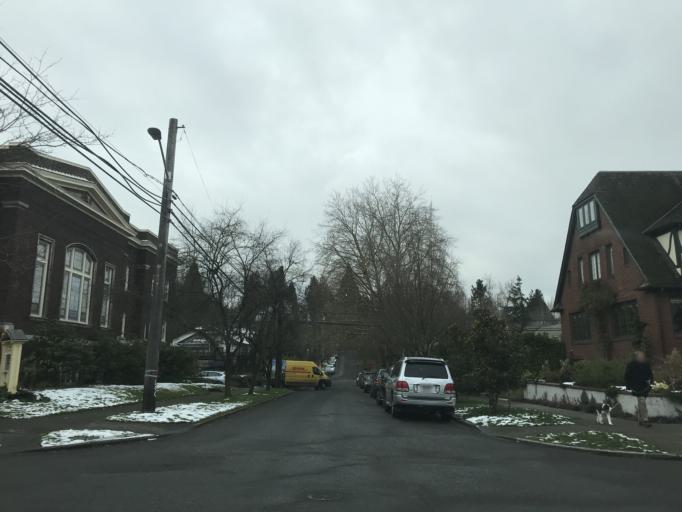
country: US
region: Washington
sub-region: King County
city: Seattle
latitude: 47.6287
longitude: -122.3060
